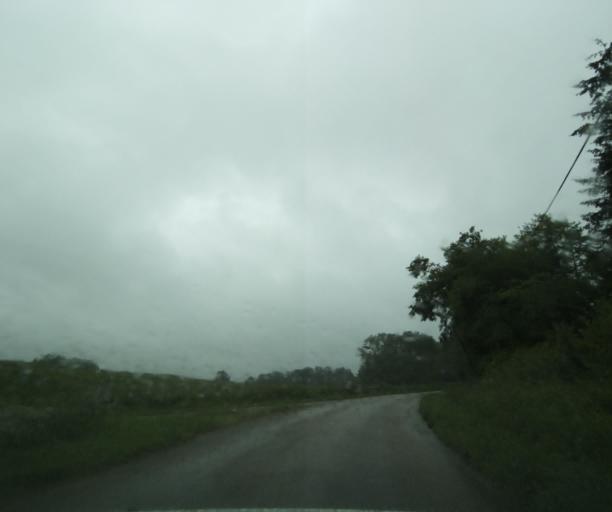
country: FR
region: Bourgogne
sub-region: Departement de Saone-et-Loire
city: Ciry-le-Noble
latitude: 46.5804
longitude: 4.3261
